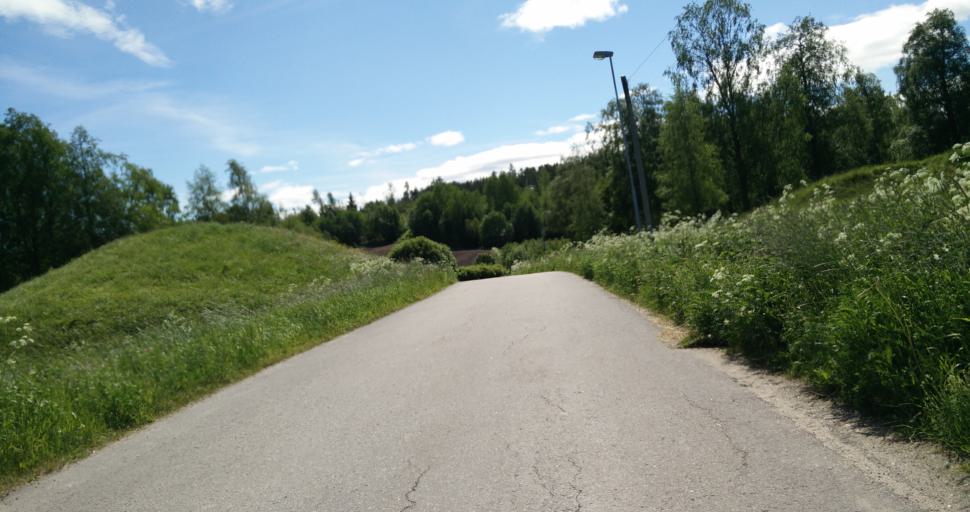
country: SE
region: Vaesternorrland
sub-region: Sundsvalls Kommun
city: Nolby
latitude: 62.2863
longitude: 17.3677
